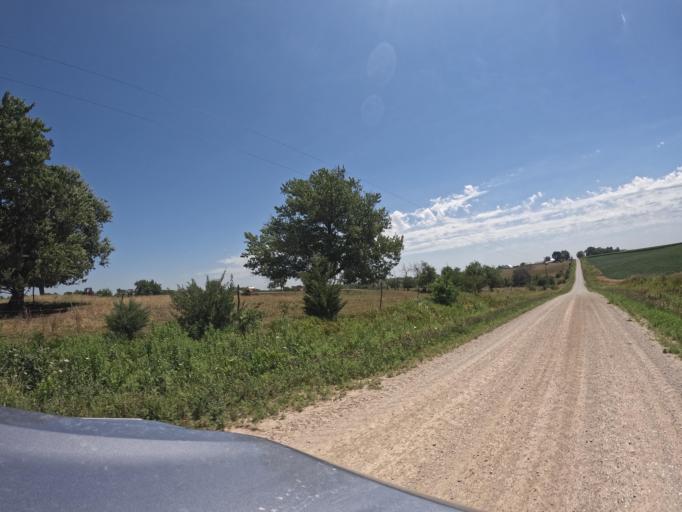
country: US
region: Iowa
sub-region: Keokuk County
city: Sigourney
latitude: 41.4205
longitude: -92.3164
